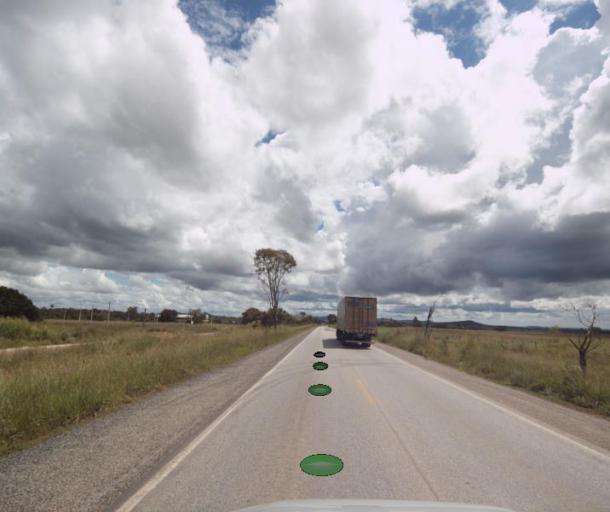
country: BR
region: Goias
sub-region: Uruacu
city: Uruacu
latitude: -14.2967
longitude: -49.1493
